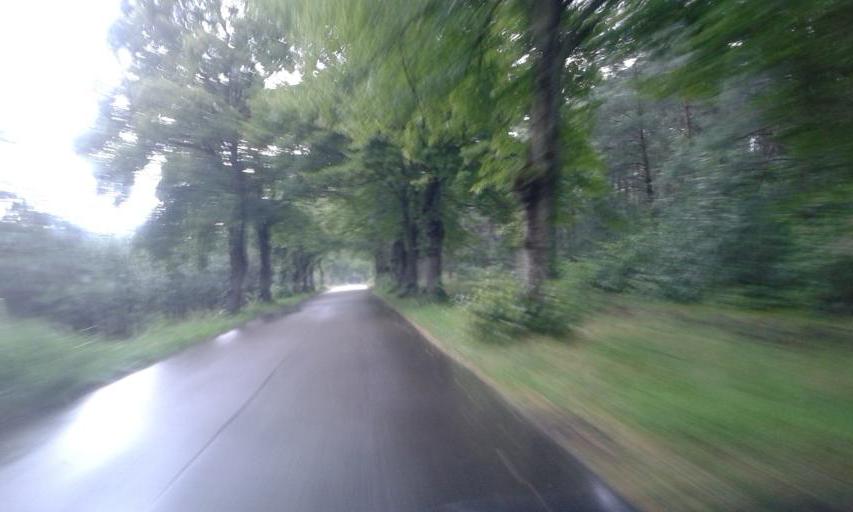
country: PL
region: West Pomeranian Voivodeship
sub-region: Powiat szczecinecki
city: Borne Sulinowo
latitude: 53.4750
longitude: 16.4962
